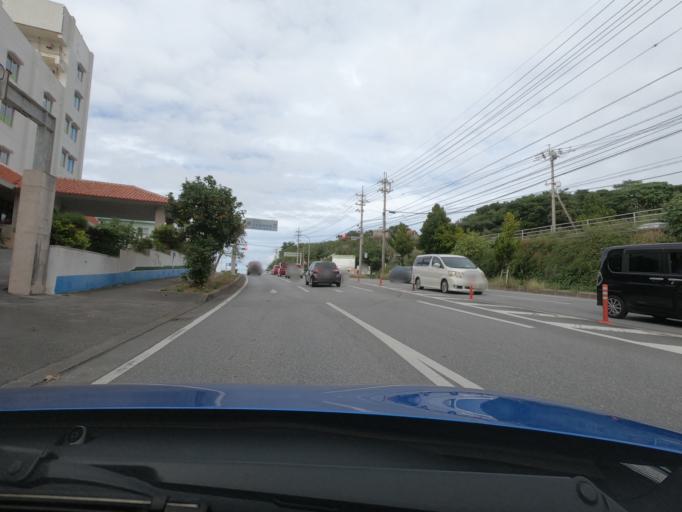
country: JP
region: Okinawa
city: Nago
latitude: 26.6635
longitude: 127.8912
